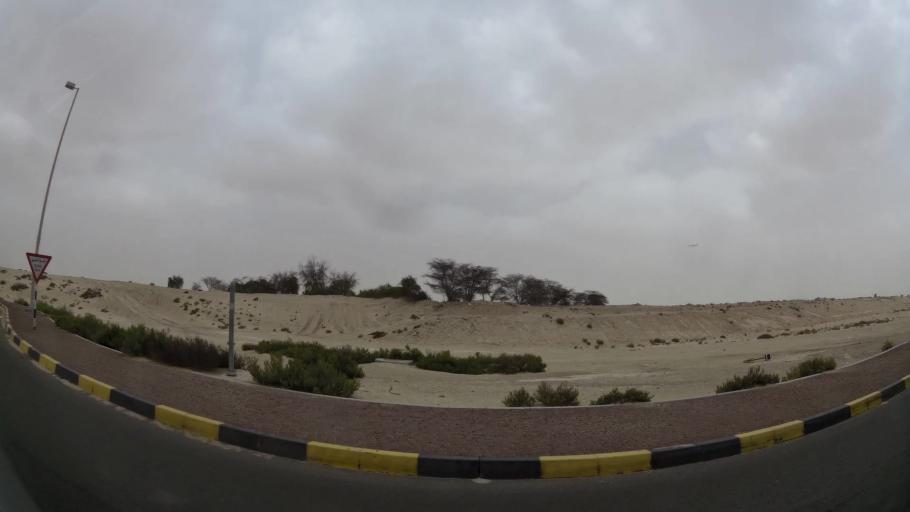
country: AE
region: Abu Dhabi
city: Abu Dhabi
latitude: 24.3995
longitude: 54.7039
